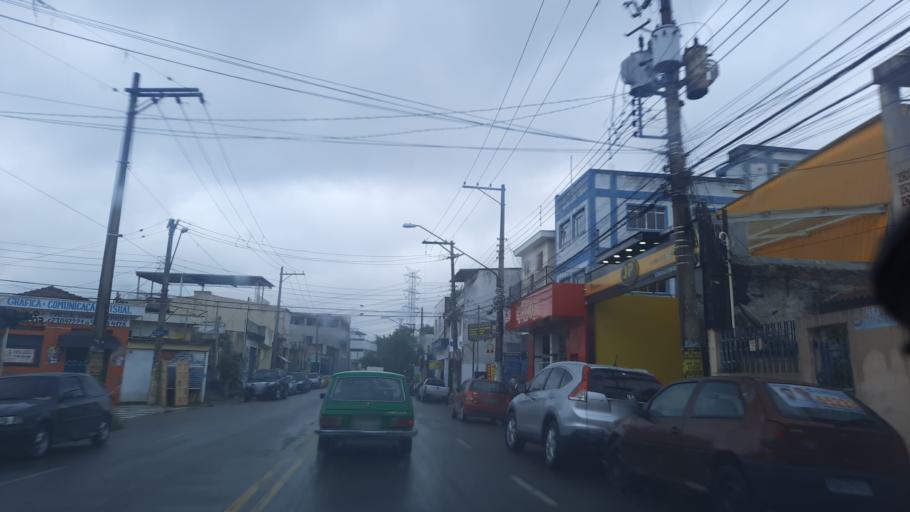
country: BR
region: Sao Paulo
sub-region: Guarulhos
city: Guarulhos
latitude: -23.4611
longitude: -46.5674
